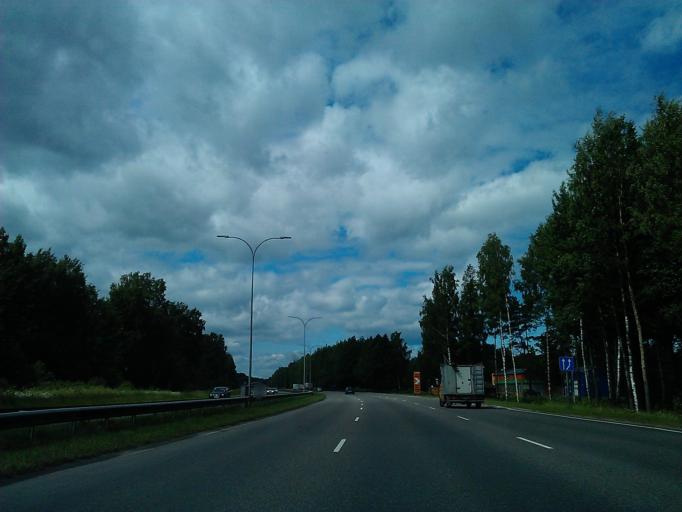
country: LV
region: Babite
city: Pinki
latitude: 56.9501
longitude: 23.9810
